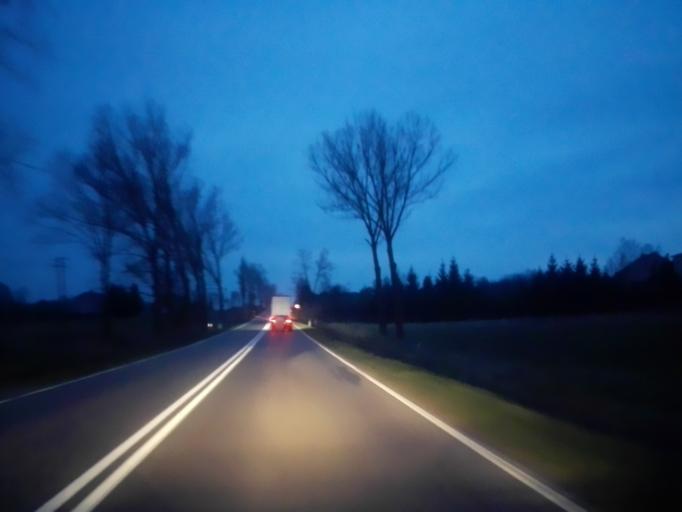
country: PL
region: Podlasie
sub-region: Lomza
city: Lomza
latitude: 53.1110
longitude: 22.0294
